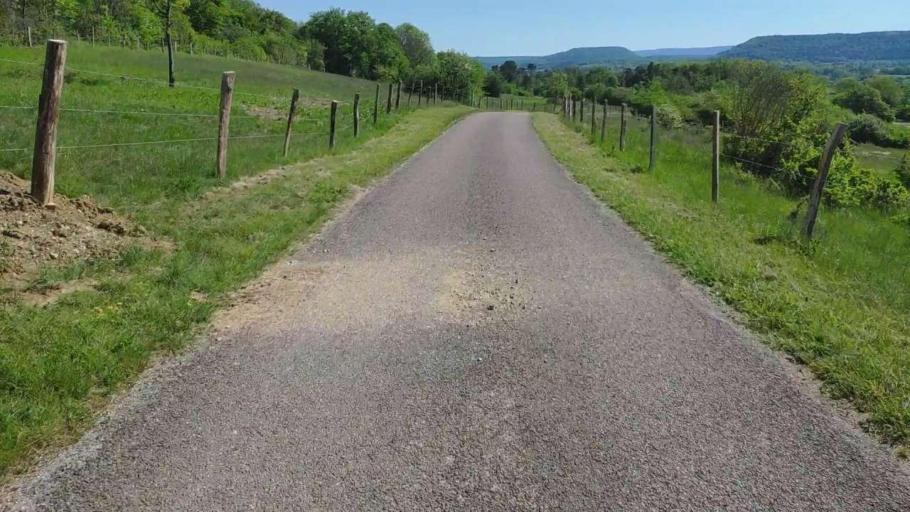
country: FR
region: Franche-Comte
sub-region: Departement du Jura
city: Clairvaux-les-Lacs
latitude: 46.7083
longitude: 5.7584
